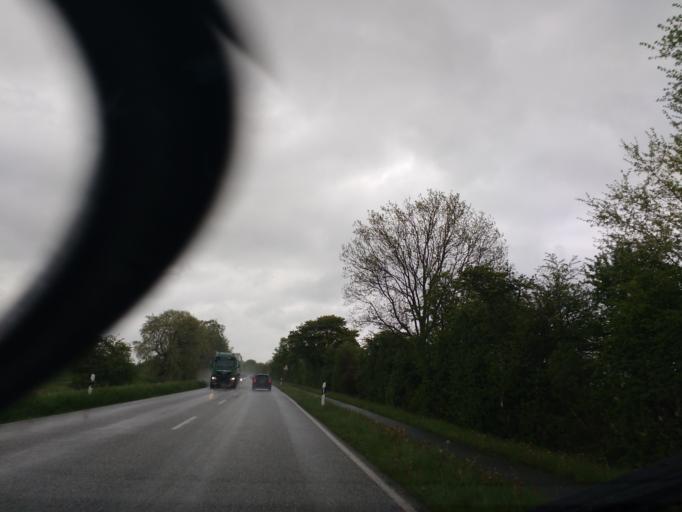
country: DE
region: Schleswig-Holstein
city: Loose
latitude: 54.5130
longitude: 9.8698
